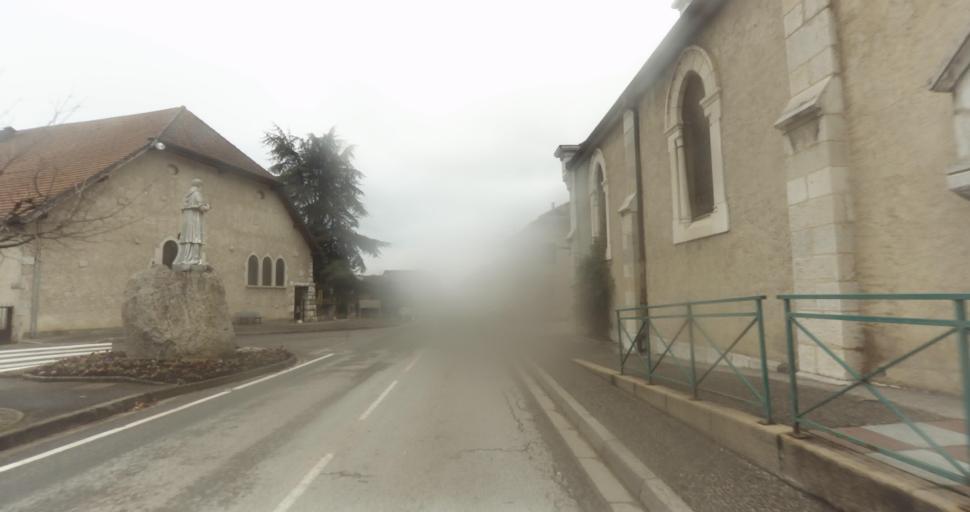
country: FR
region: Rhone-Alpes
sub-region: Departement de la Haute-Savoie
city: Thorens-Glieres
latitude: 45.9968
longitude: 6.2471
